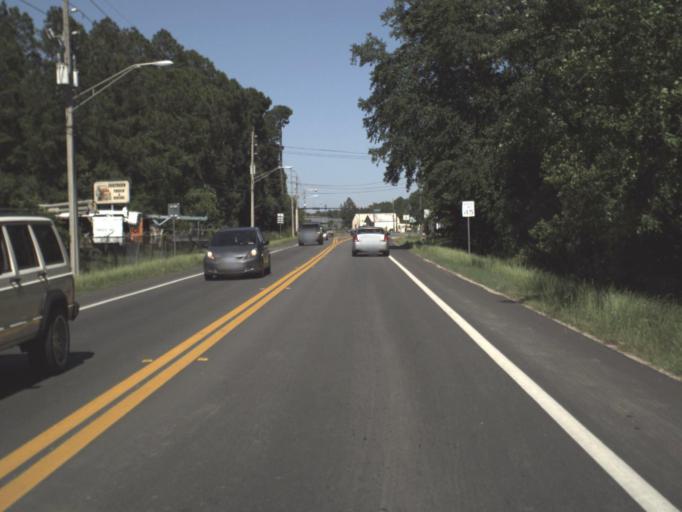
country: US
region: Florida
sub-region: Duval County
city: Jacksonville
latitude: 30.3199
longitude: -81.7960
